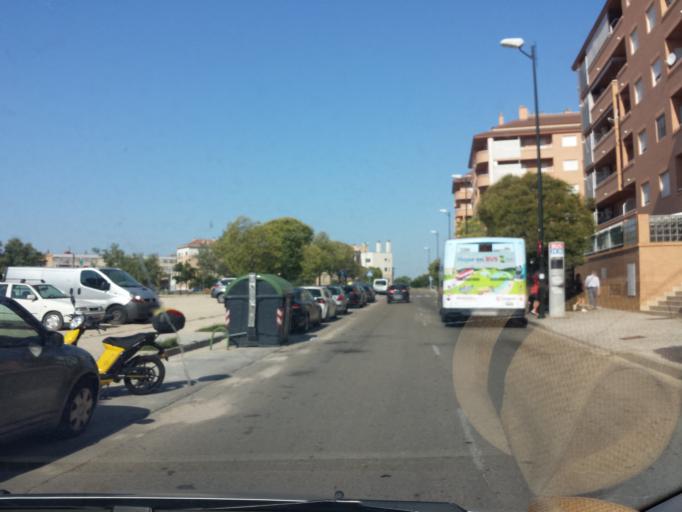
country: ES
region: Aragon
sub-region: Provincia de Zaragoza
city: Oliver-Valdefierro, Oliver, Valdefierro
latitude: 41.6416
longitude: -0.9343
